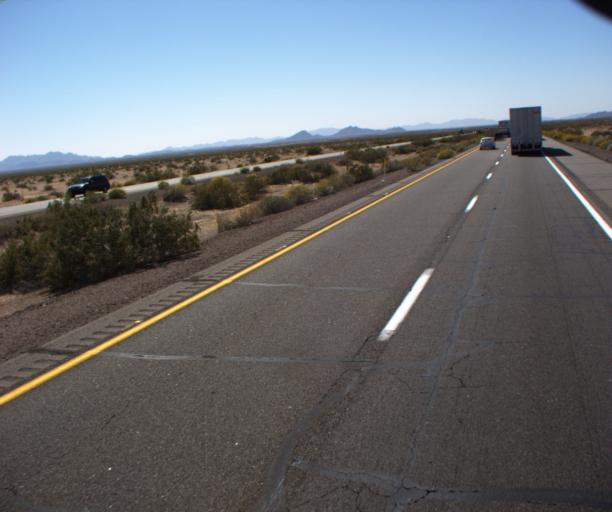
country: US
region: Arizona
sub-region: Yuma County
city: Wellton
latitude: 32.7134
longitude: -113.8238
